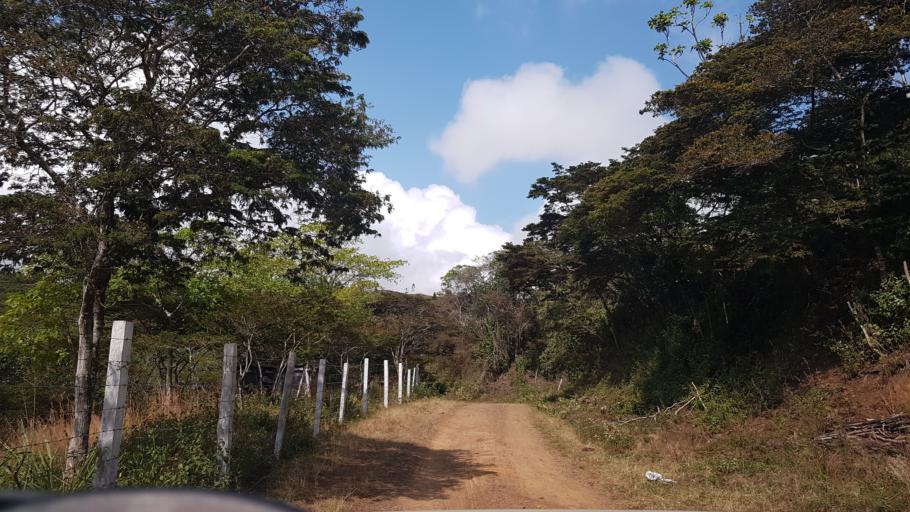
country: CO
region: Valle del Cauca
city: Yumbo
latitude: 3.6537
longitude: -76.5159
